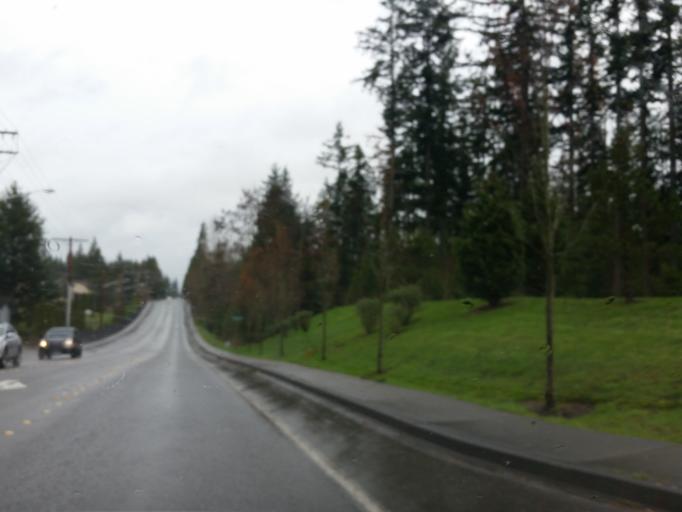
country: US
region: Washington
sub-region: Snohomish County
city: Mill Creek
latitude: 47.9000
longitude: -122.1853
